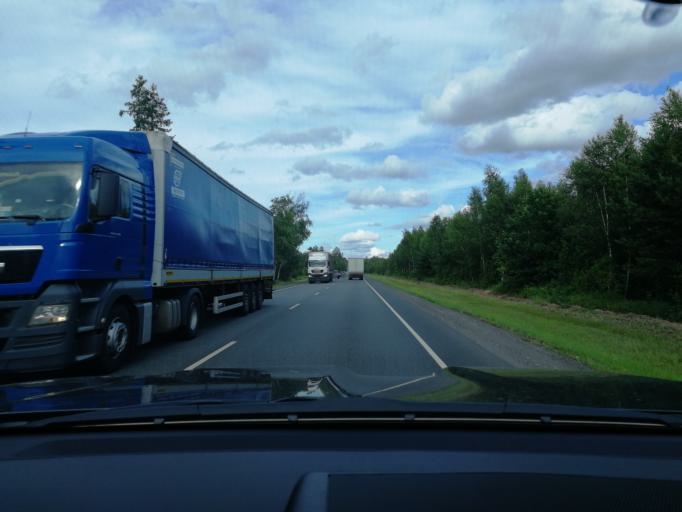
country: RU
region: Moskovskaya
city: Mikhnevo
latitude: 55.0710
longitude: 37.8576
